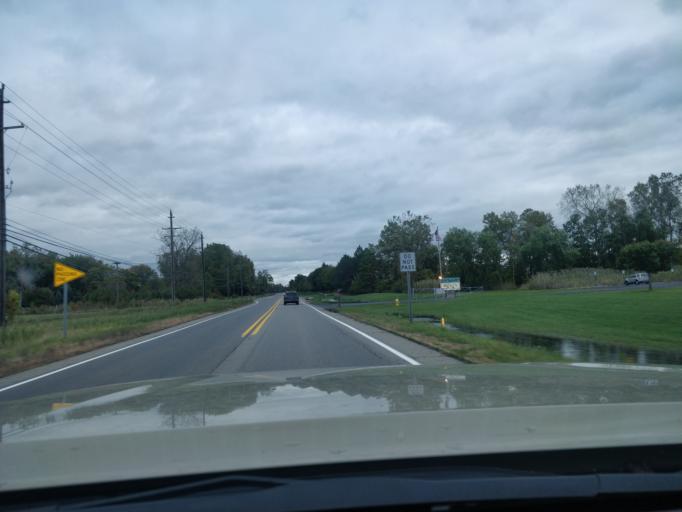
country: US
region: Michigan
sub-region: Wayne County
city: Taylor
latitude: 42.1818
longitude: -83.2978
